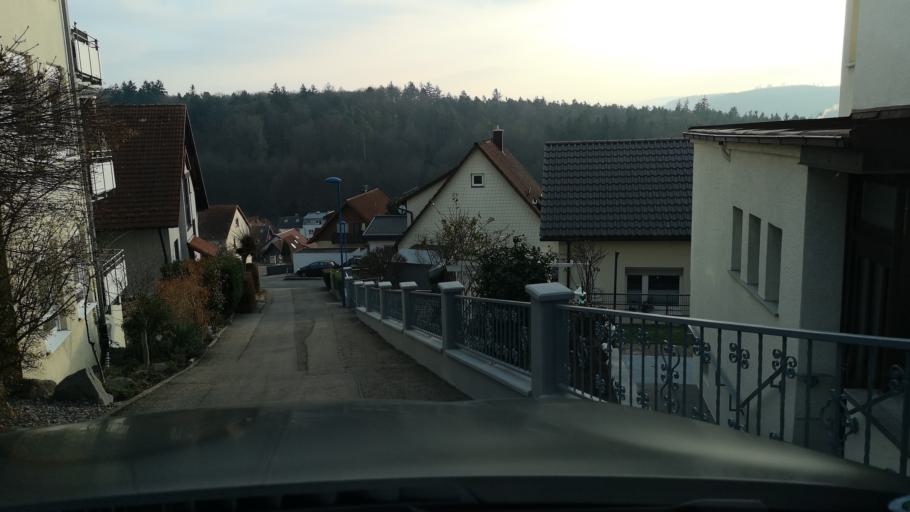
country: DE
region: Baden-Wuerttemberg
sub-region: Karlsruhe Region
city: Ettlingen
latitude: 48.9324
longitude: 8.4571
